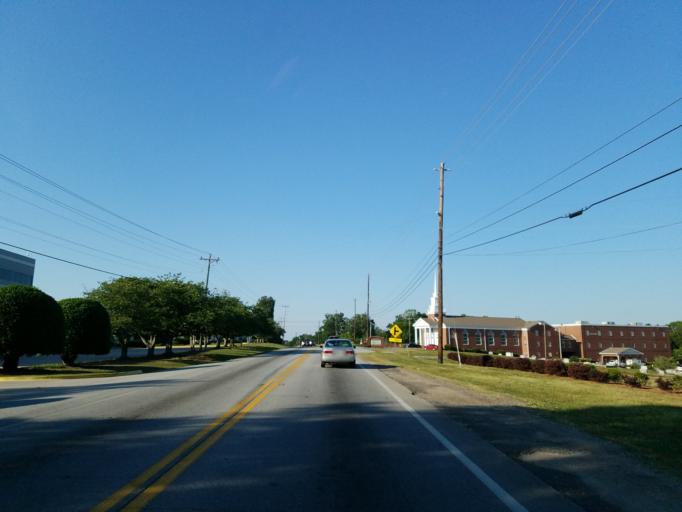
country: US
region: Georgia
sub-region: Douglas County
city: Lithia Springs
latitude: 33.7786
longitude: -84.7049
